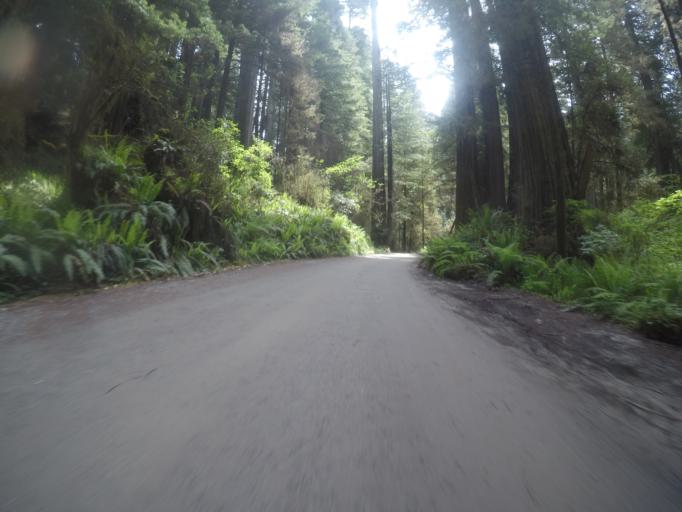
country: US
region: California
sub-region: Del Norte County
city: Bertsch-Oceanview
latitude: 41.7663
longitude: -124.1143
